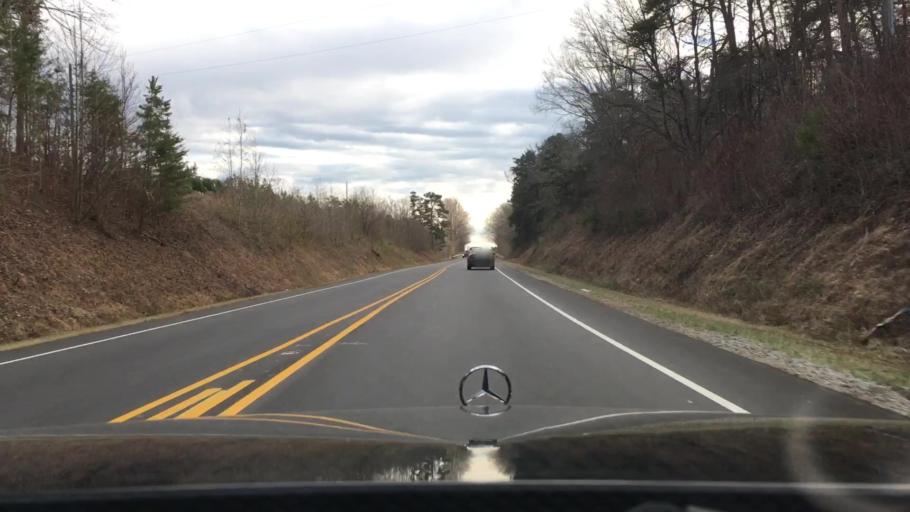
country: US
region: North Carolina
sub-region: Caswell County
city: Yanceyville
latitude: 36.4383
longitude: -79.3619
